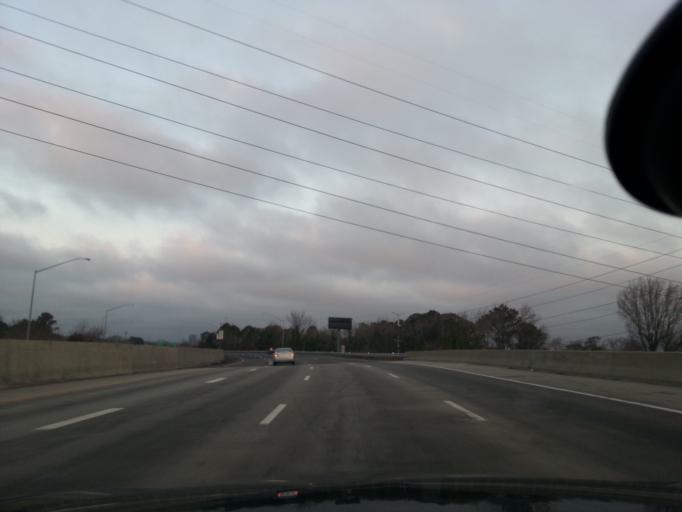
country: US
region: Virginia
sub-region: City of Chesapeake
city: Chesapeake
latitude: 36.8461
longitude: -76.2434
